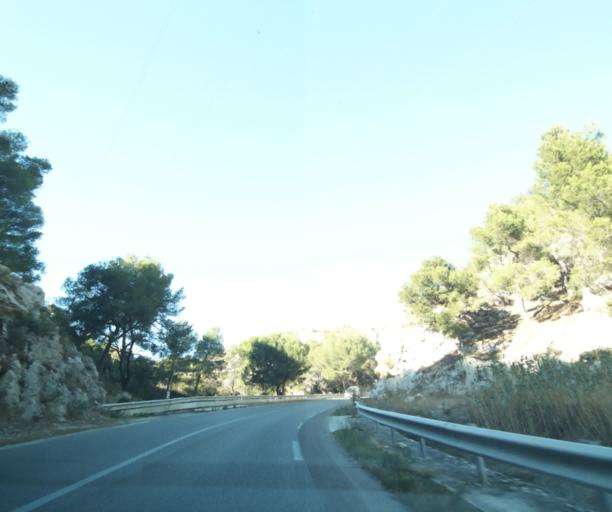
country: FR
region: Provence-Alpes-Cote d'Azur
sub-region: Departement des Bouches-du-Rhone
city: Le Rove
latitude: 43.3643
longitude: 5.2648
